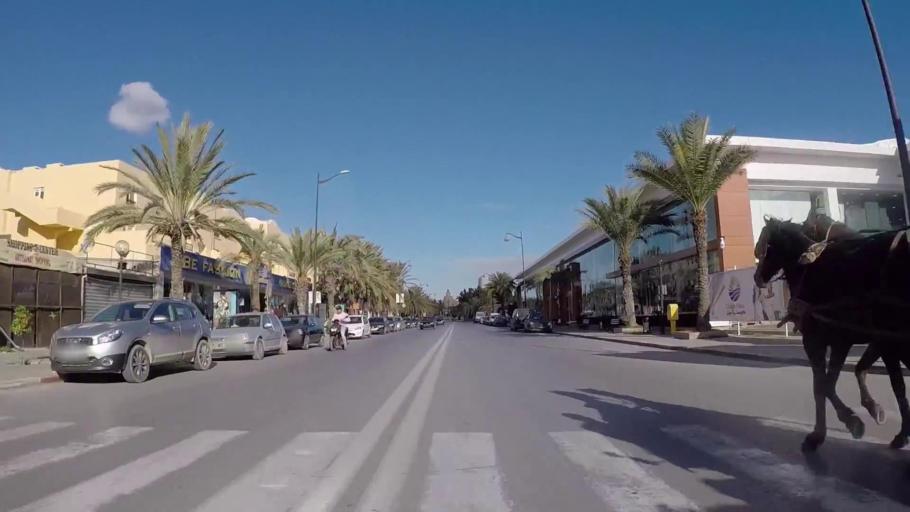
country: TN
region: Nabul
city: Al Hammamat
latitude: 36.3683
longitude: 10.5358
